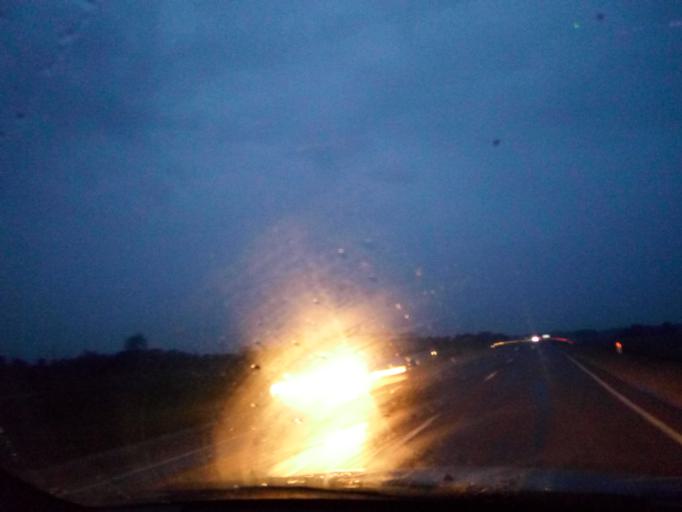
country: RU
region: Primorskiy
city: Dal'nerechensk
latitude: 45.9108
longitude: 133.7628
